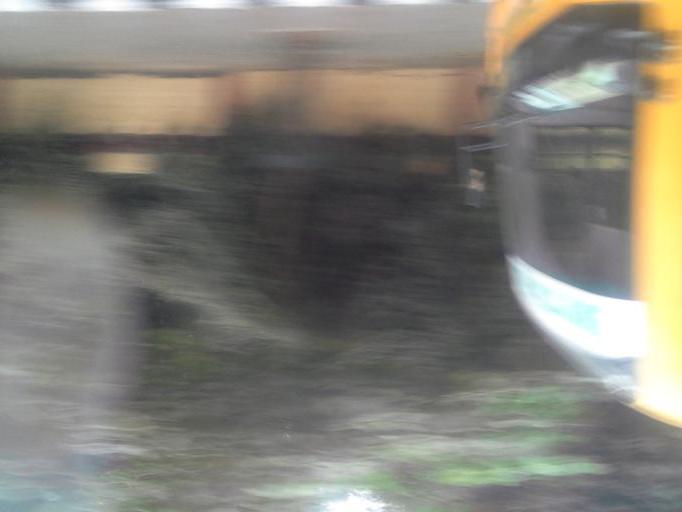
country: IN
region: Karnataka
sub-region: Bangalore Urban
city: Bangalore
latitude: 12.9790
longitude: 77.6029
